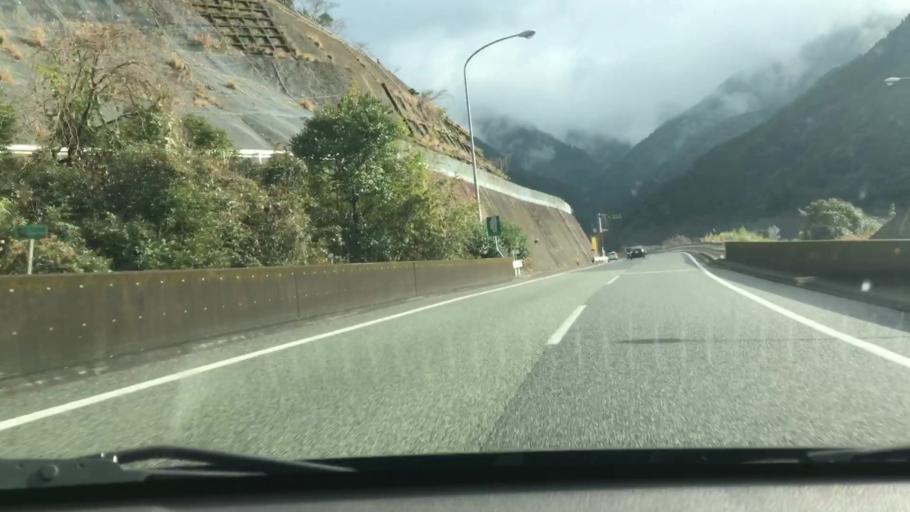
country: JP
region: Kumamoto
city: Yatsushiro
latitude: 32.3990
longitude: 130.7024
